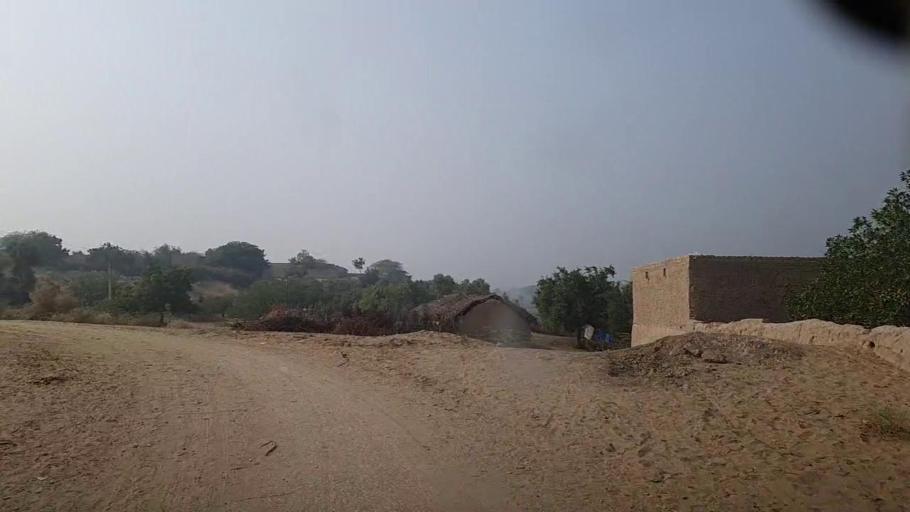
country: PK
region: Sindh
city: Bozdar
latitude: 27.0686
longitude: 68.6325
